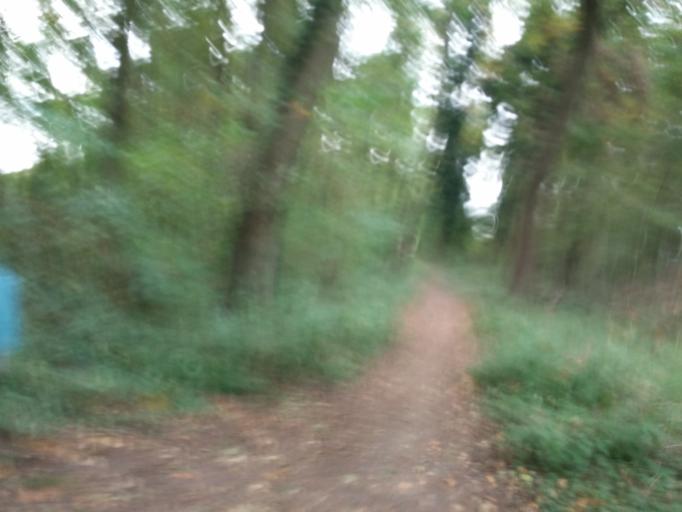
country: DE
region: North Rhine-Westphalia
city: Dorsten
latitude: 51.6378
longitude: 7.0169
